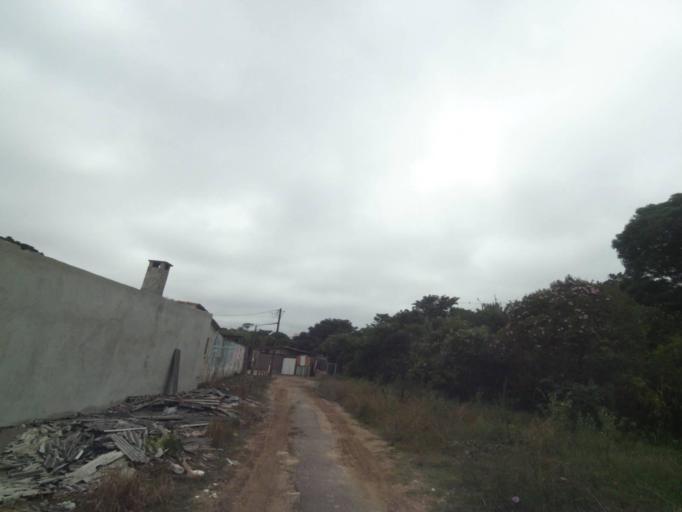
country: BR
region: Parana
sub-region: Curitiba
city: Curitiba
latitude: -25.4988
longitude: -49.3487
